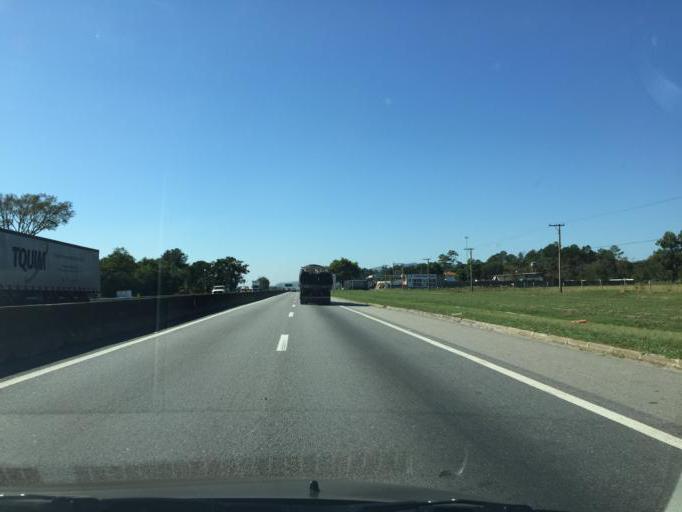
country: BR
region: Sao Paulo
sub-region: Pindamonhangaba
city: Pindamonhangaba
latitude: -22.9273
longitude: -45.3550
